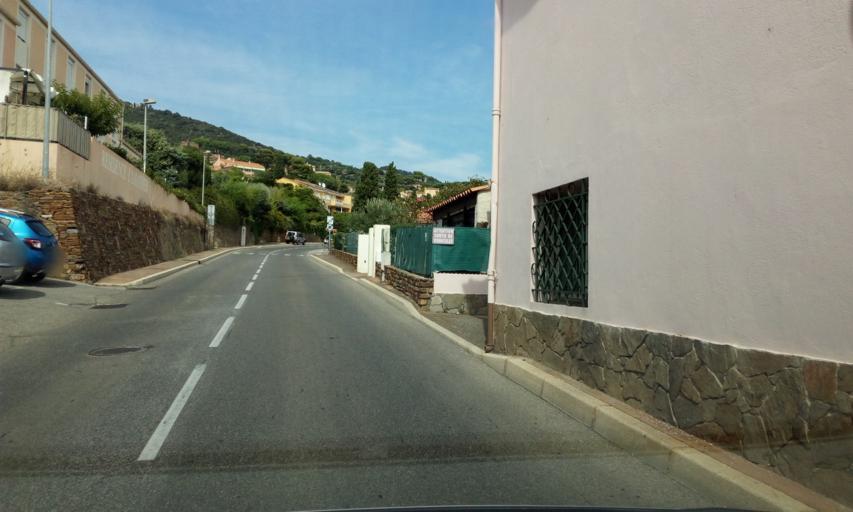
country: FR
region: Provence-Alpes-Cote d'Azur
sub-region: Departement du Var
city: Bormes-les-Mimosas
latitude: 43.1450
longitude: 6.3389
